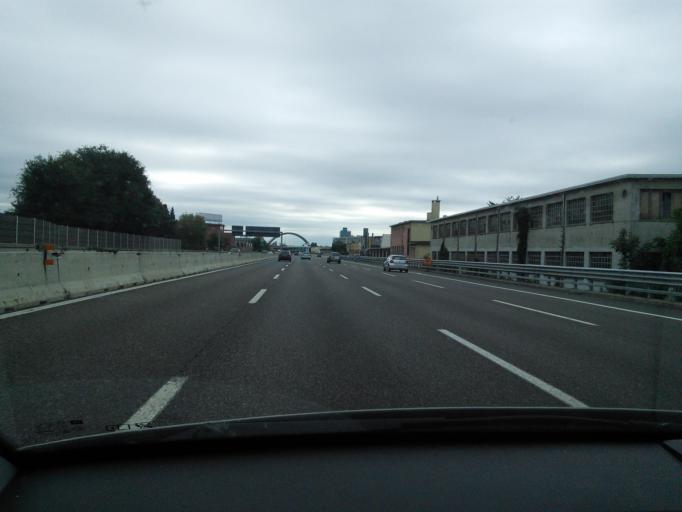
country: IT
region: Lombardy
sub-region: Citta metropolitana di Milano
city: Baranzate
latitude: 45.5241
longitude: 9.1048
